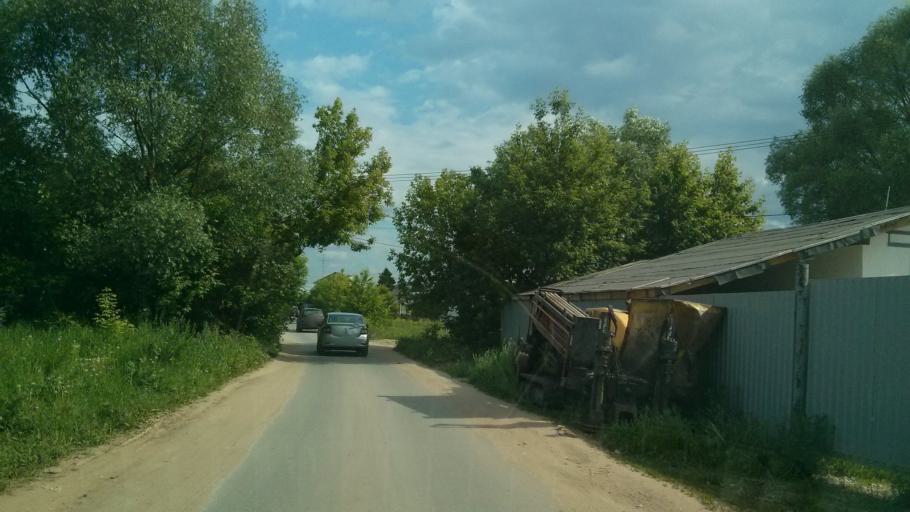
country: RU
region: Nizjnij Novgorod
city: Afonino
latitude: 56.2808
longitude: 44.1021
